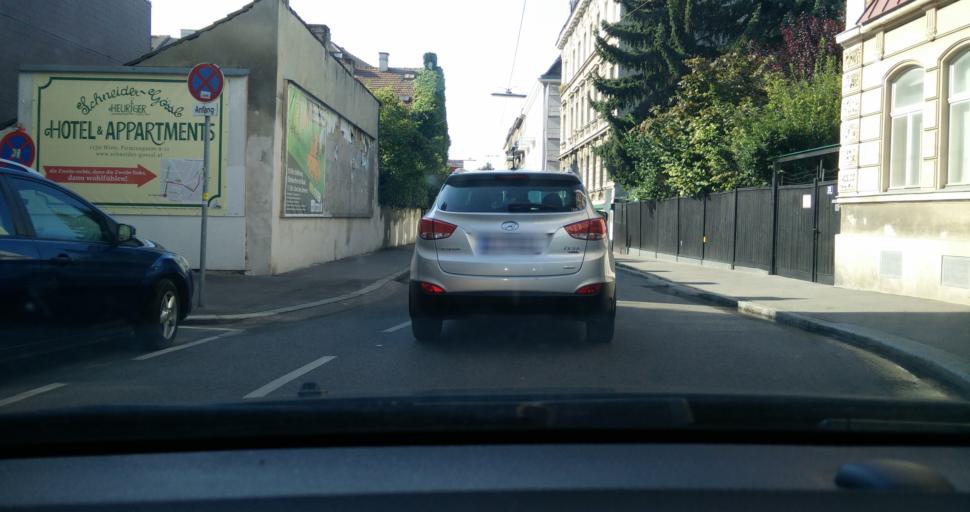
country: AT
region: Lower Austria
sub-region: Politischer Bezirk Modling
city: Perchtoldsdorf
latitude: 48.1921
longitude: 16.2739
